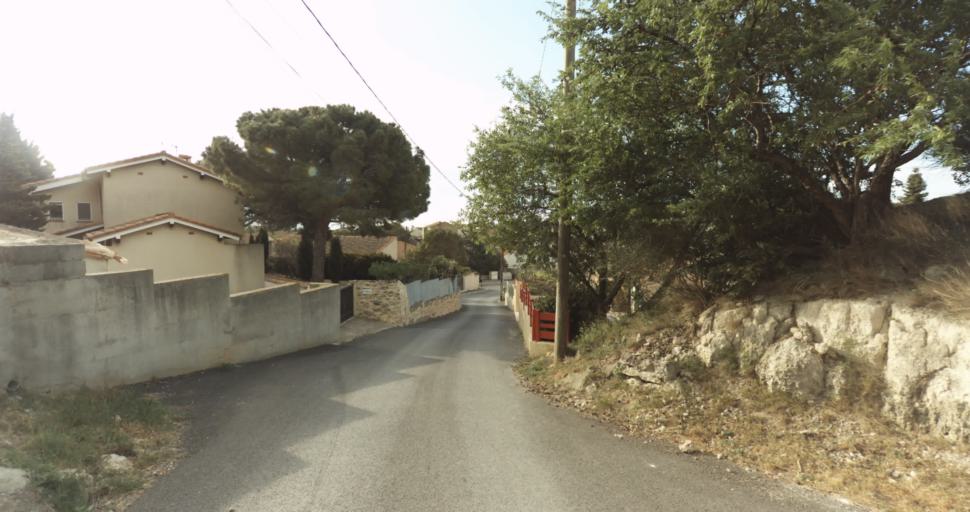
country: FR
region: Languedoc-Roussillon
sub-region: Departement de l'Aude
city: Leucate
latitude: 42.9123
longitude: 3.0250
